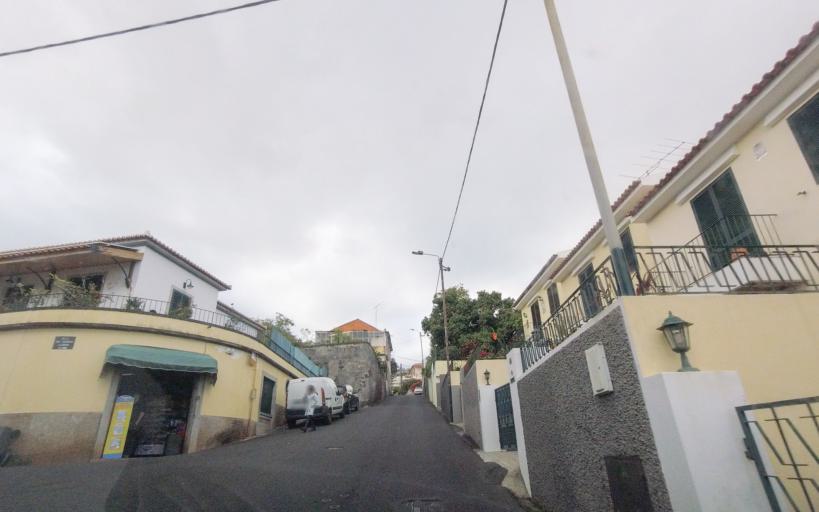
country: PT
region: Madeira
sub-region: Funchal
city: Nossa Senhora do Monte
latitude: 32.6536
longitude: -16.8980
